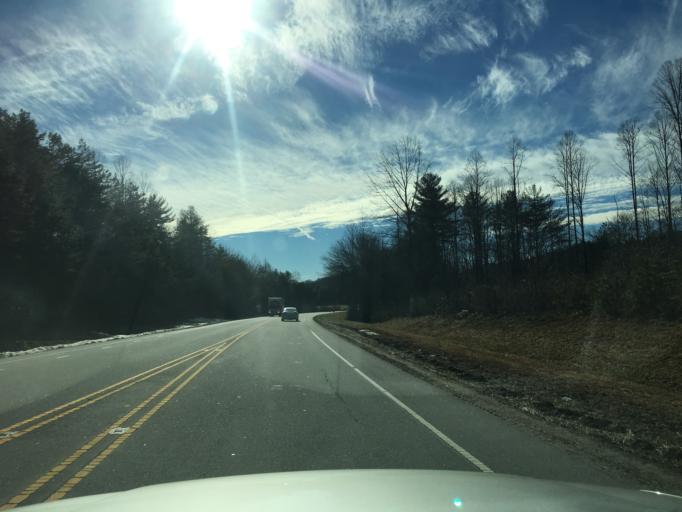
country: US
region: North Carolina
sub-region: Transylvania County
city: Brevard
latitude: 35.1940
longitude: -82.7837
